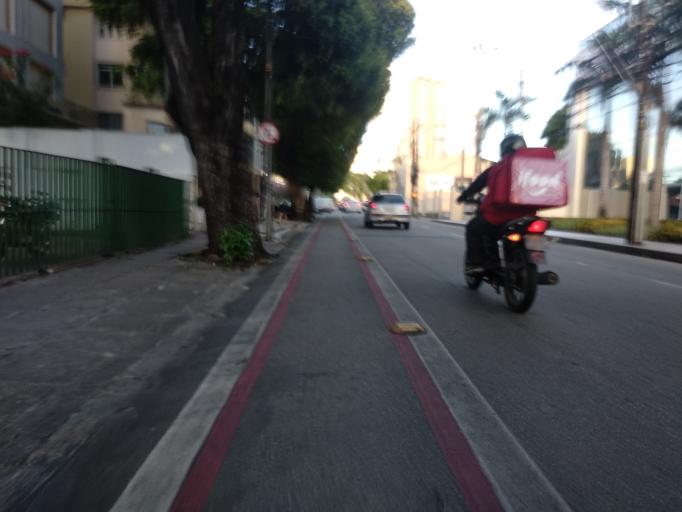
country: BR
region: Ceara
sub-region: Fortaleza
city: Fortaleza
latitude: -3.7305
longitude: -38.5158
